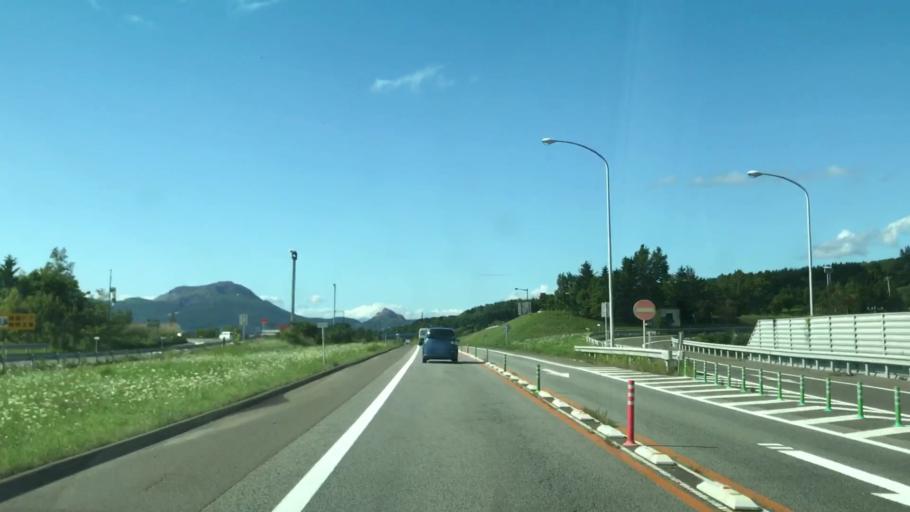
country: JP
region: Hokkaido
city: Date
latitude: 42.4642
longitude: 140.9098
